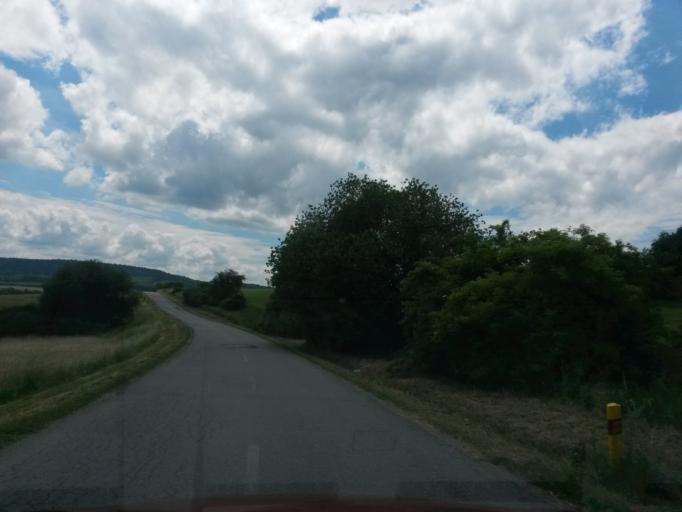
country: SK
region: Kosicky
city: Gelnica
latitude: 48.9345
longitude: 21.0454
